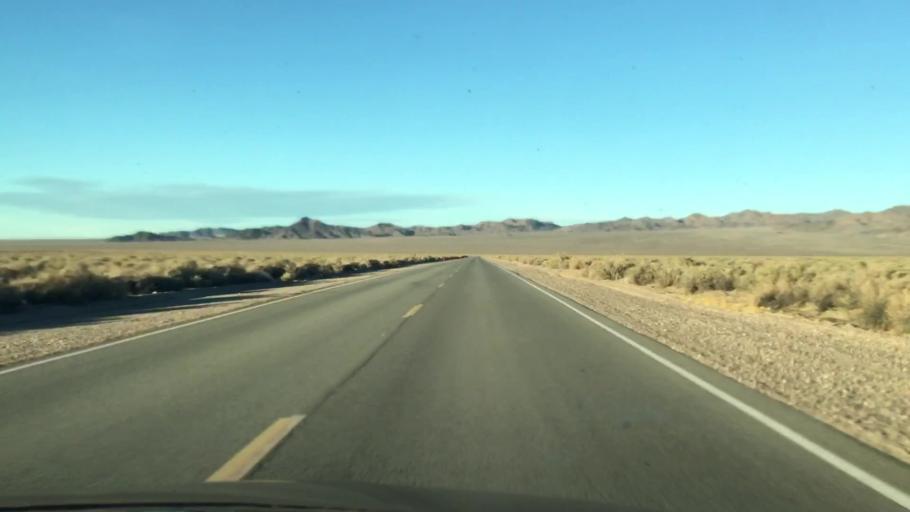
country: US
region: California
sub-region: San Bernardino County
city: Fort Irwin
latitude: 35.3186
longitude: -116.0829
